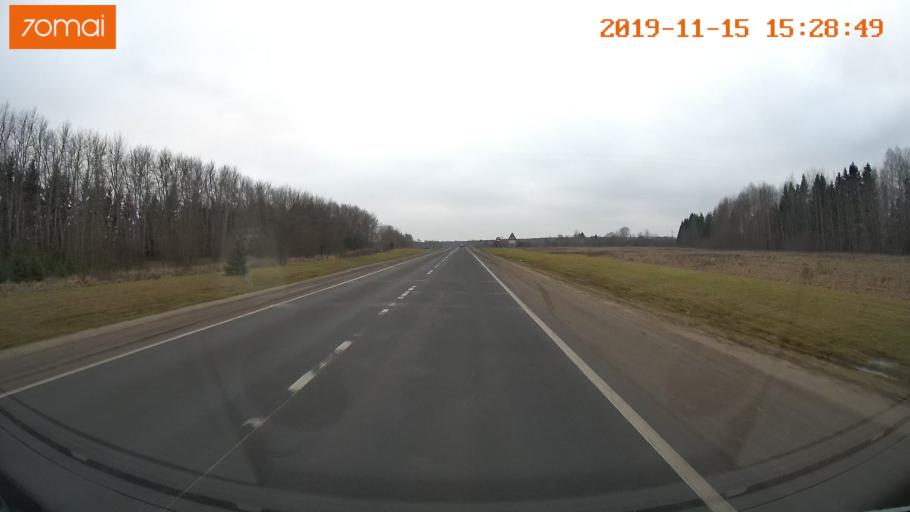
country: RU
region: Jaroslavl
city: Danilov
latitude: 58.1278
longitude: 40.1293
